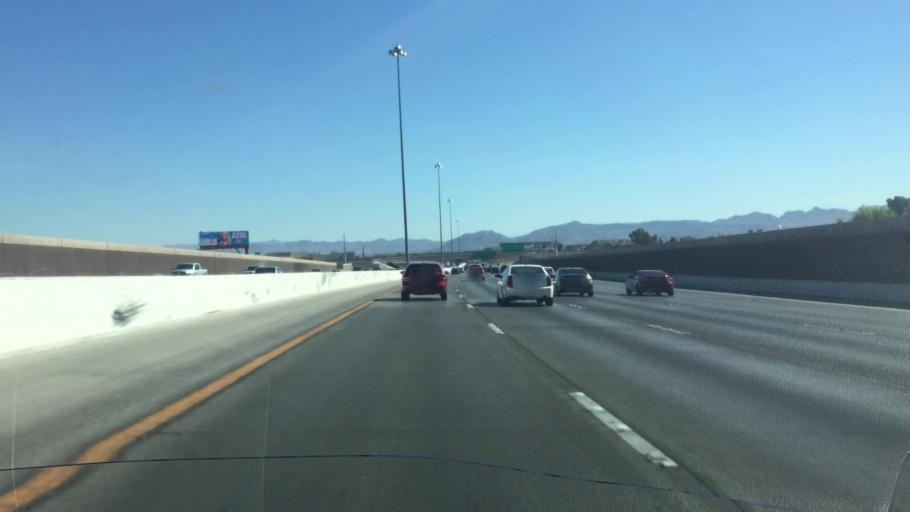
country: US
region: Nevada
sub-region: Clark County
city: Paradise
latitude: 36.0680
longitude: -115.1956
